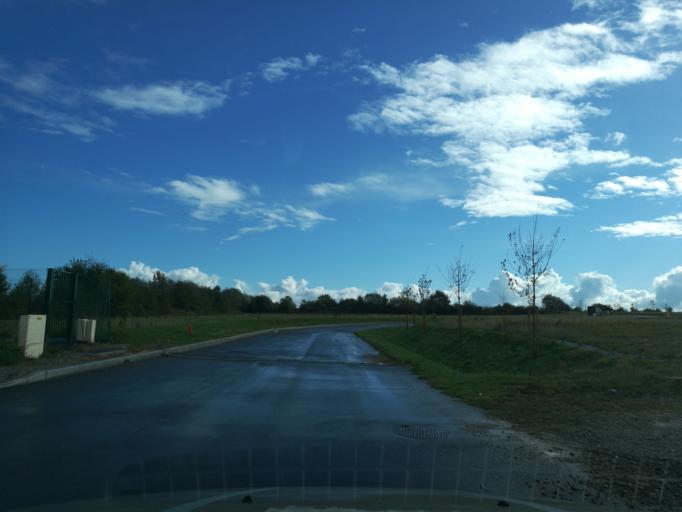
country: FR
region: Brittany
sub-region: Departement d'Ille-et-Vilaine
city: Bedee
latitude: 48.1878
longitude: -1.9385
